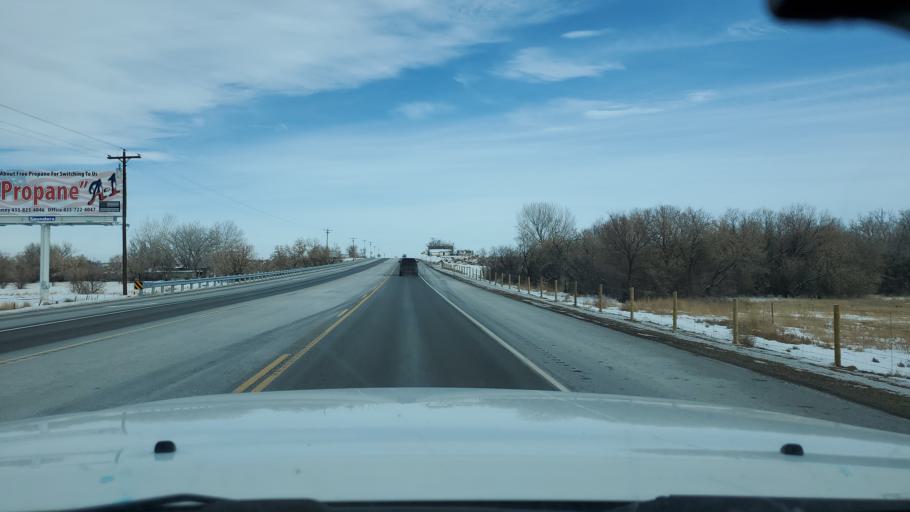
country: US
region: Utah
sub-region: Duchesne County
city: Roosevelt
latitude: 40.3019
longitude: -109.8394
